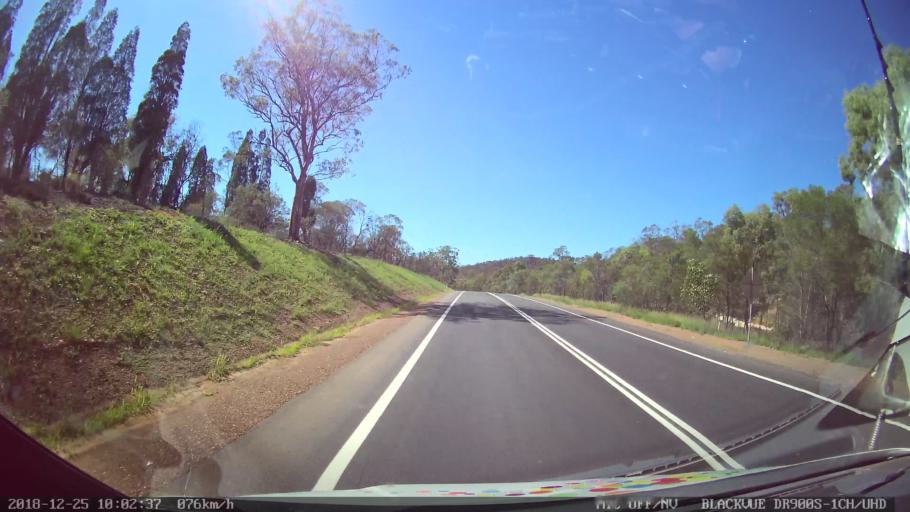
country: AU
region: New South Wales
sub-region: Upper Hunter Shire
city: Merriwa
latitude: -32.2205
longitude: 150.4645
